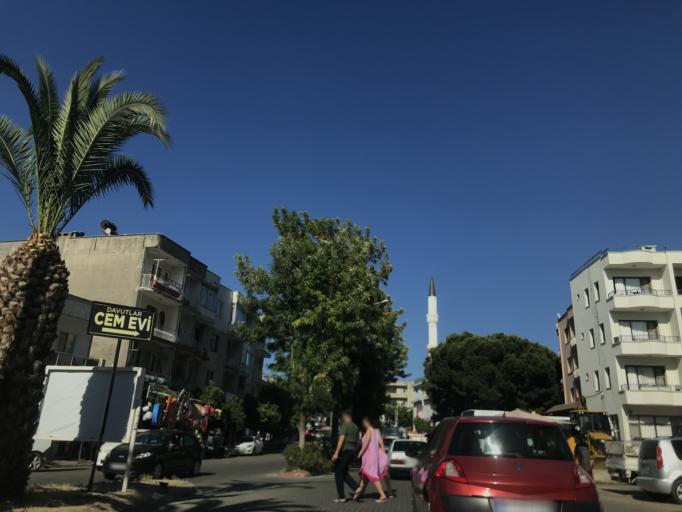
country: TR
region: Aydin
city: Davutlar
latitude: 37.7334
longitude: 27.2930
